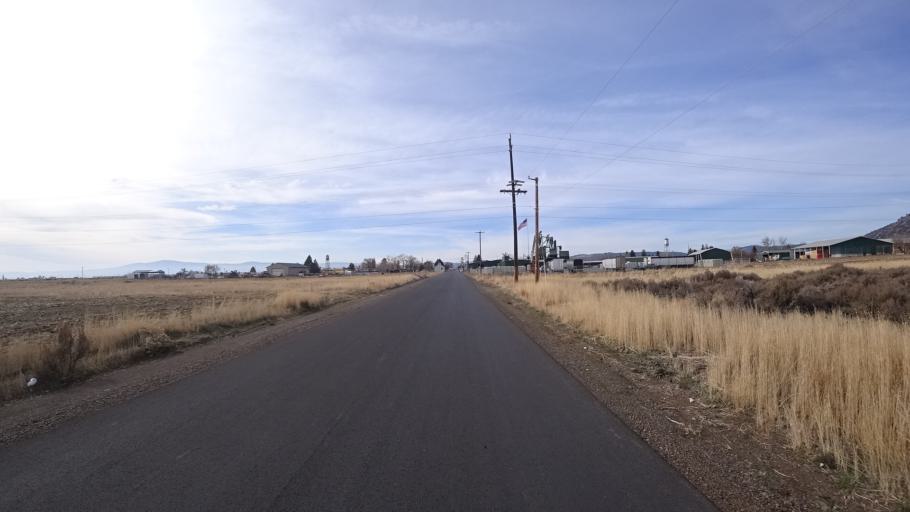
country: US
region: Oregon
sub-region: Klamath County
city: Klamath Falls
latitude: 41.9627
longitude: -121.9128
